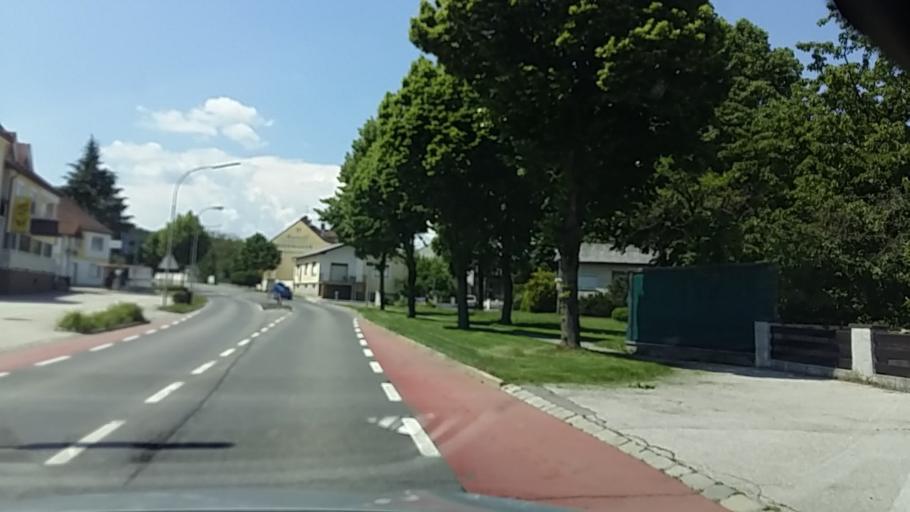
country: AT
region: Burgenland
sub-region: Politischer Bezirk Oberpullendorf
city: Piringsdorf
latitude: 47.4466
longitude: 16.4148
